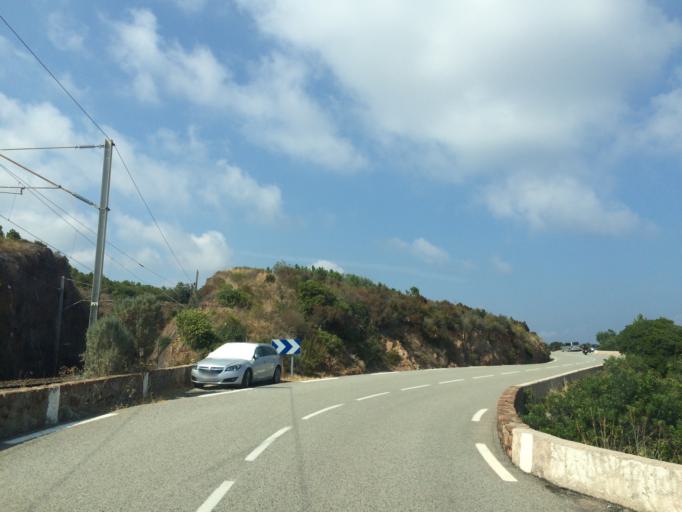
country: FR
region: Provence-Alpes-Cote d'Azur
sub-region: Departement des Alpes-Maritimes
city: Theoule-sur-Mer
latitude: 43.4538
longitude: 6.9202
